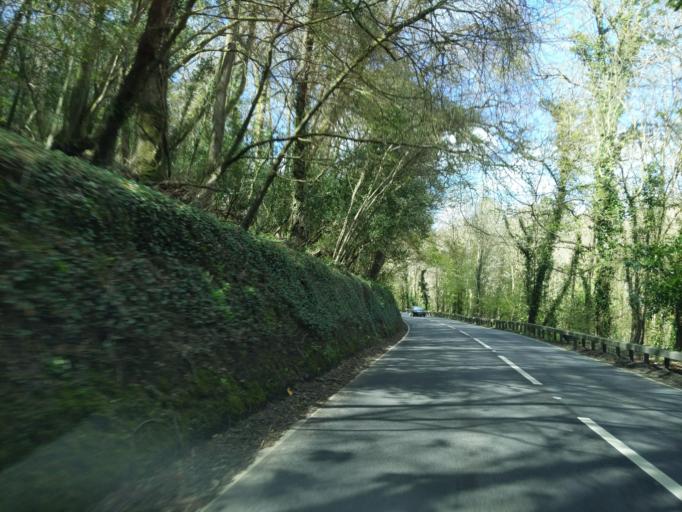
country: GB
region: England
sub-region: Cornwall
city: Wadebridge
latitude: 50.5062
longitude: -4.7812
